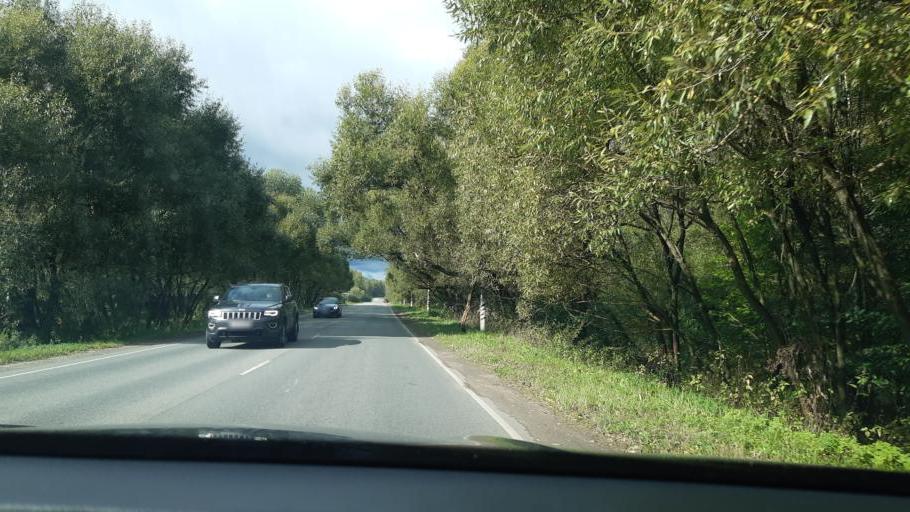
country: RU
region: Moskovskaya
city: Melikhovo
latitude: 55.1145
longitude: 37.6430
